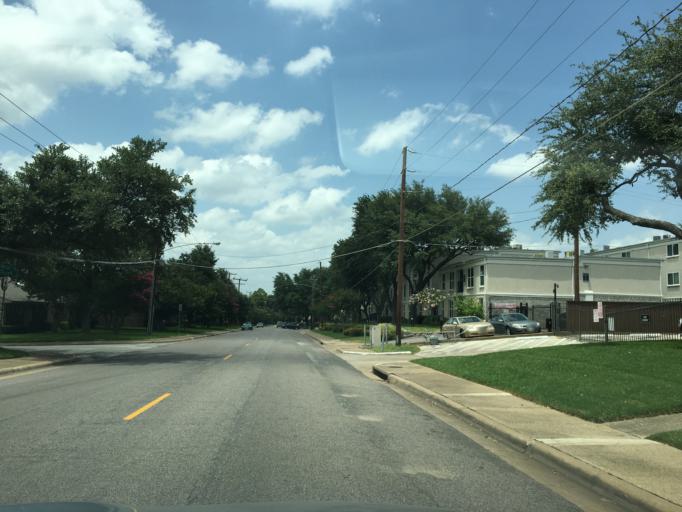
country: US
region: Texas
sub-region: Dallas County
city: University Park
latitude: 32.8914
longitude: -96.7750
